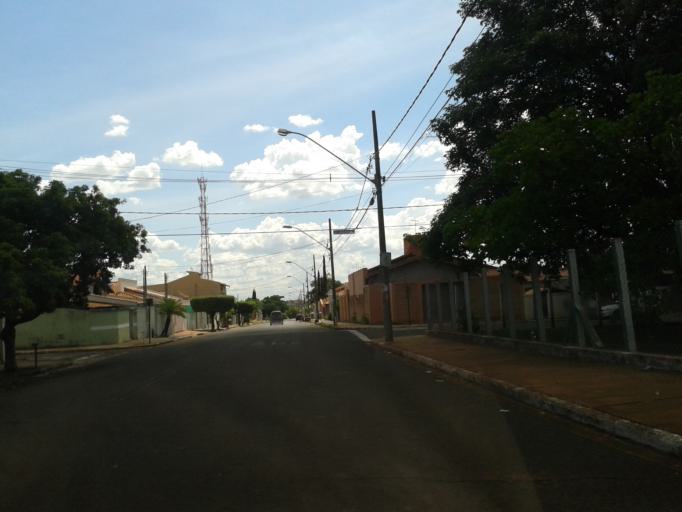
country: BR
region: Minas Gerais
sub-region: Ituiutaba
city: Ituiutaba
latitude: -18.9852
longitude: -49.4635
